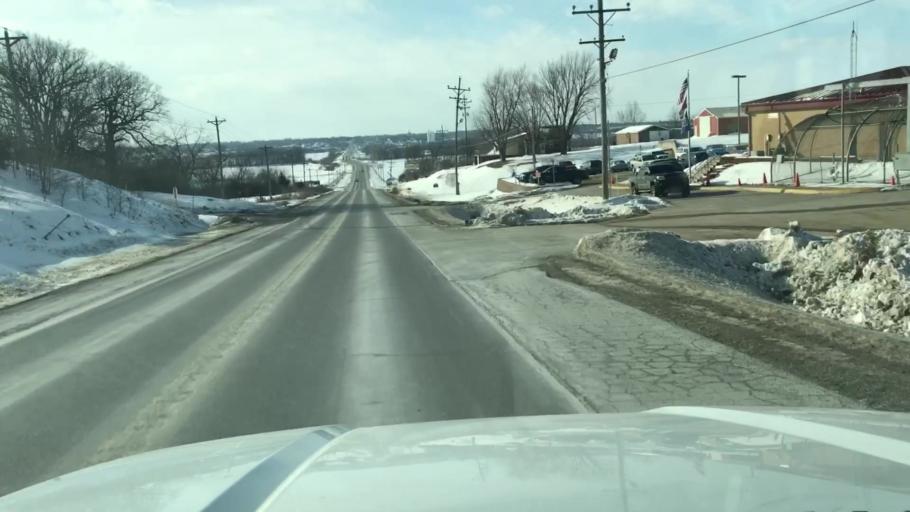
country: US
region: Missouri
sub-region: Nodaway County
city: Maryville
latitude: 40.3448
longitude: -94.8153
